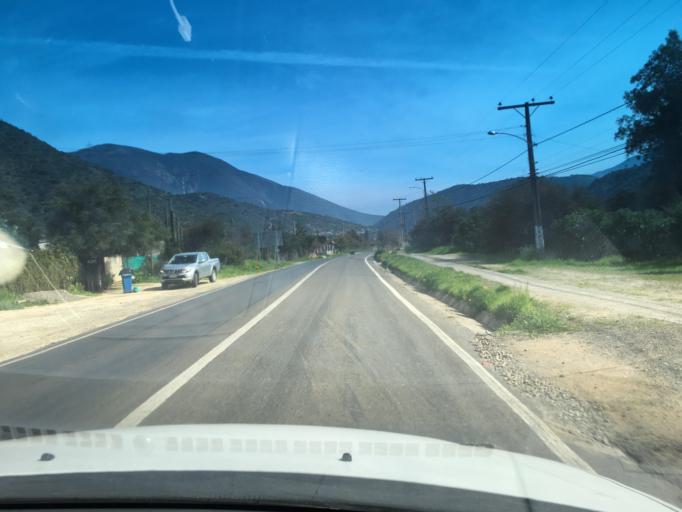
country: CL
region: Valparaiso
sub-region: Provincia de Marga Marga
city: Limache
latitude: -33.0574
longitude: -71.0851
